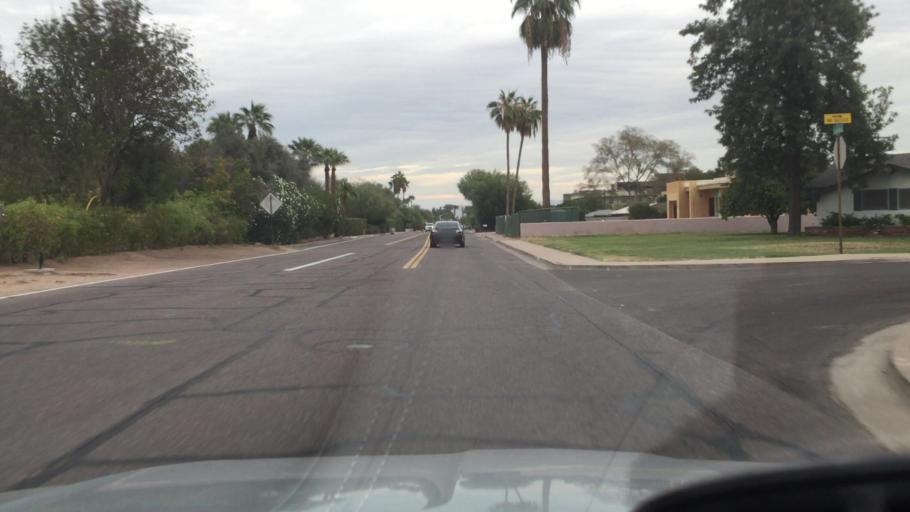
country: US
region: Arizona
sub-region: Maricopa County
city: Paradise Valley
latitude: 33.5094
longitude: -111.9335
